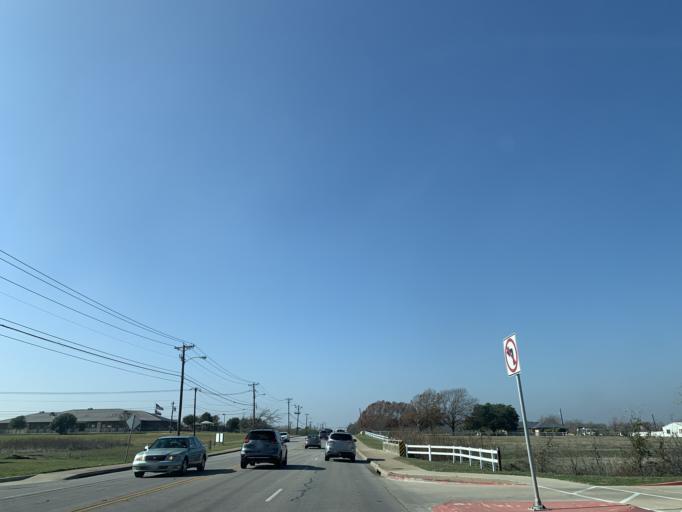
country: US
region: Texas
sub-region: Williamson County
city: Round Rock
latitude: 30.4964
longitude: -97.6472
